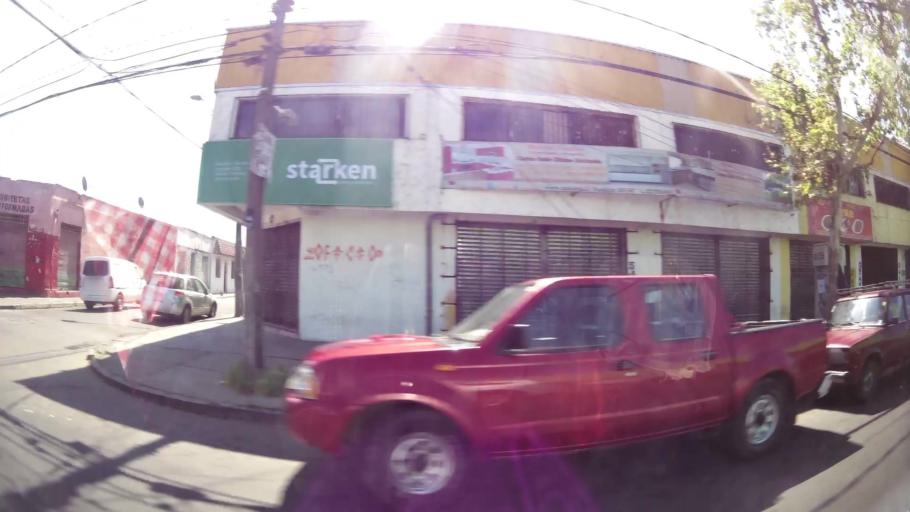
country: CL
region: Santiago Metropolitan
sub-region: Provincia de Santiago
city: Santiago
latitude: -33.4725
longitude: -70.6373
